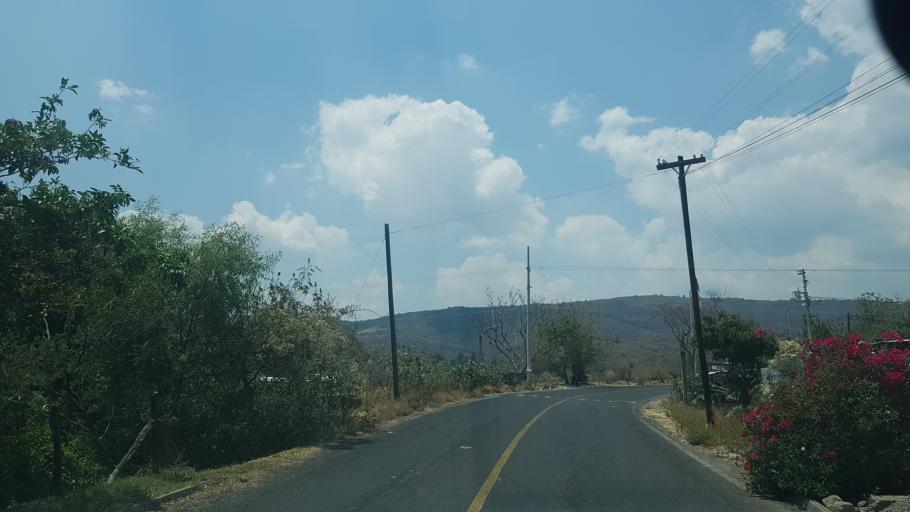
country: MX
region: Puebla
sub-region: Atzitzihuacan
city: Santiago Atzitzihuacan
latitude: 18.8405
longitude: -98.5836
